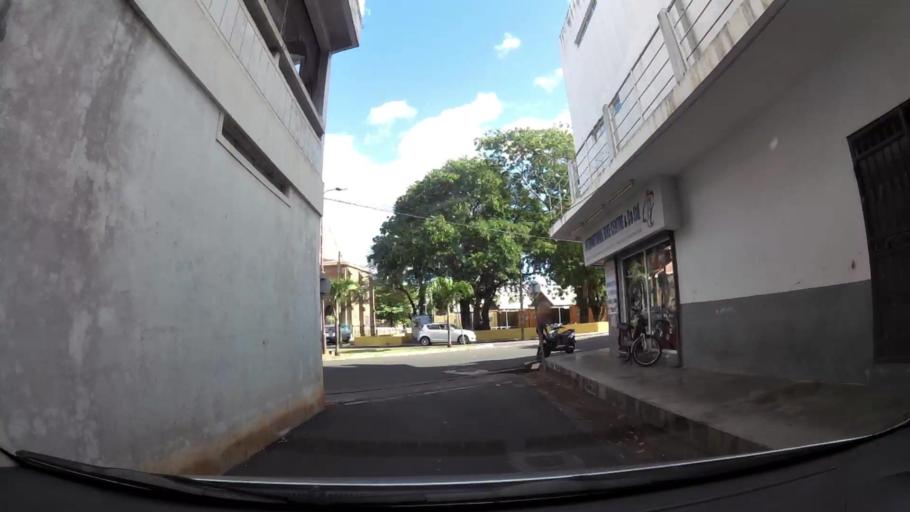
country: MU
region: Port Louis
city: Port Louis
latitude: -20.1549
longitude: 57.5149
